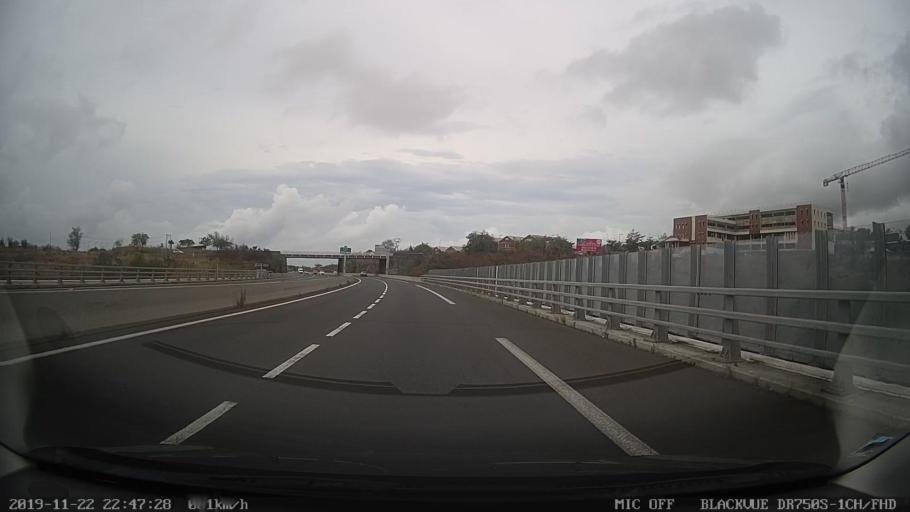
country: RE
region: Reunion
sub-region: Reunion
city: Saint-Paul
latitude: -21.0448
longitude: 55.2499
